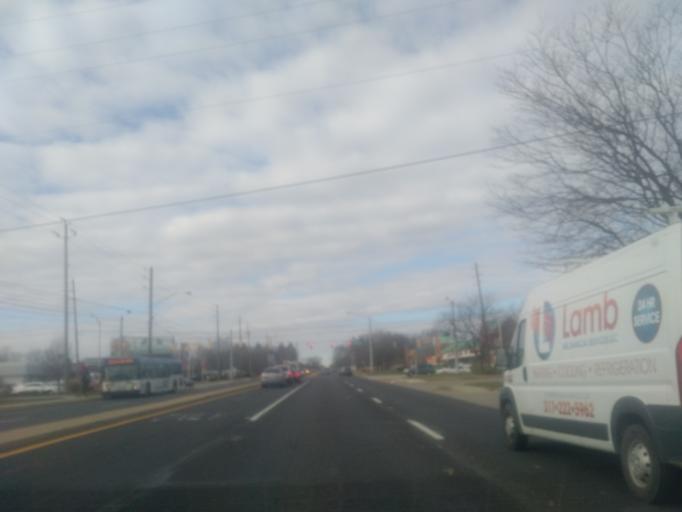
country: US
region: Indiana
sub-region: Marion County
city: Meridian Hills
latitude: 39.9123
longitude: -86.1829
